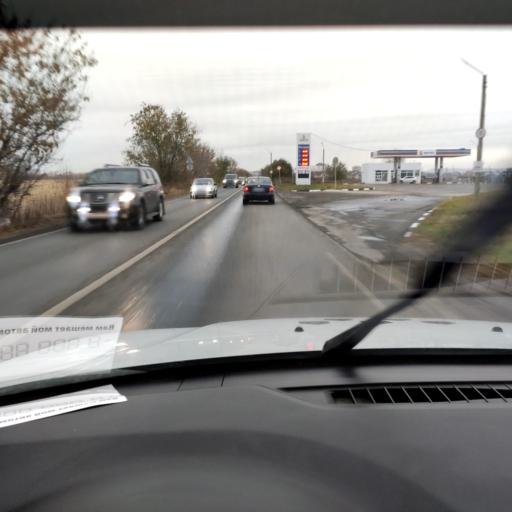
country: RU
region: Samara
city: Podstepki
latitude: 53.5198
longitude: 49.2245
